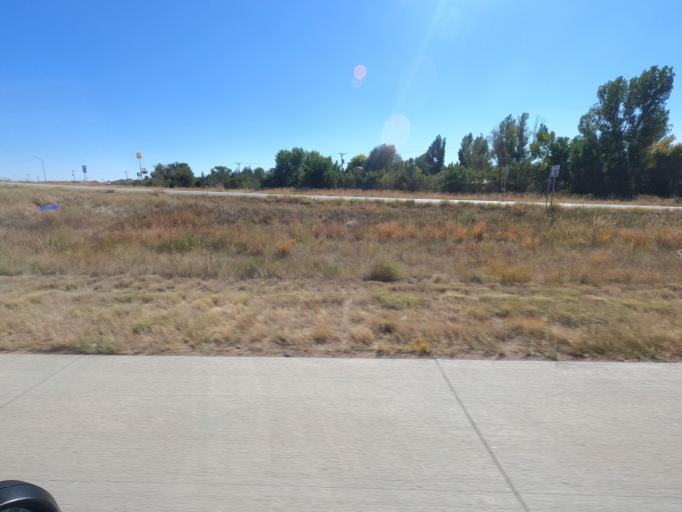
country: US
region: Colorado
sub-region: Morgan County
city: Brush
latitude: 40.2685
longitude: -103.6233
